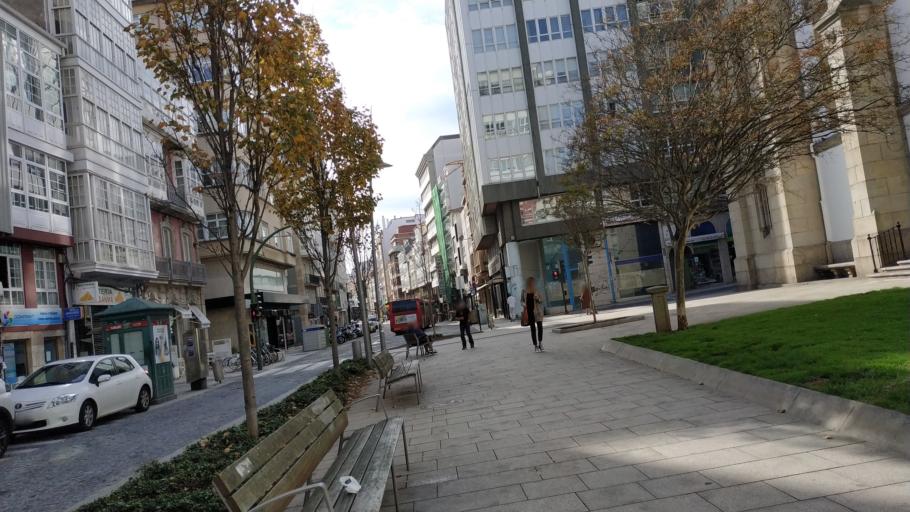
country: ES
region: Galicia
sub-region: Provincia da Coruna
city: A Coruna
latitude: 43.3708
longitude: -8.4016
